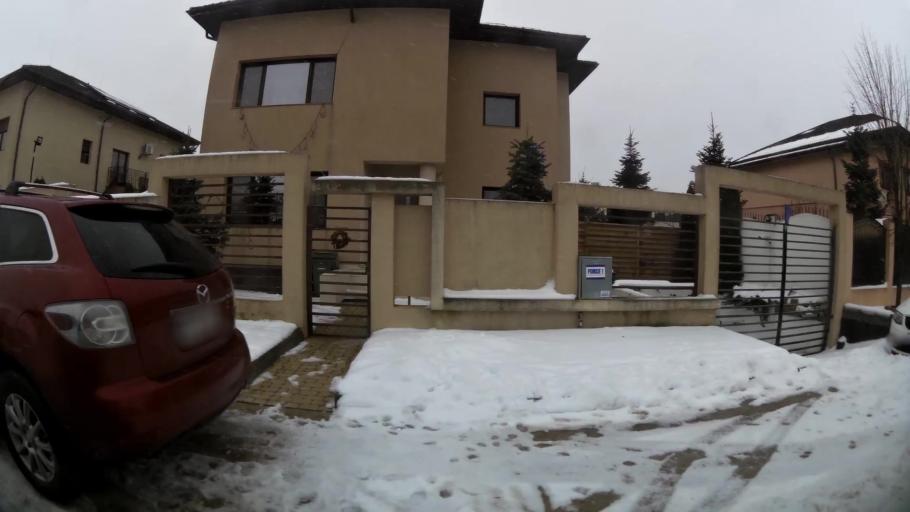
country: RO
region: Ilfov
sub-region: Comuna Mogosoaia
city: Mogosoaia
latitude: 44.5076
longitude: 26.0137
